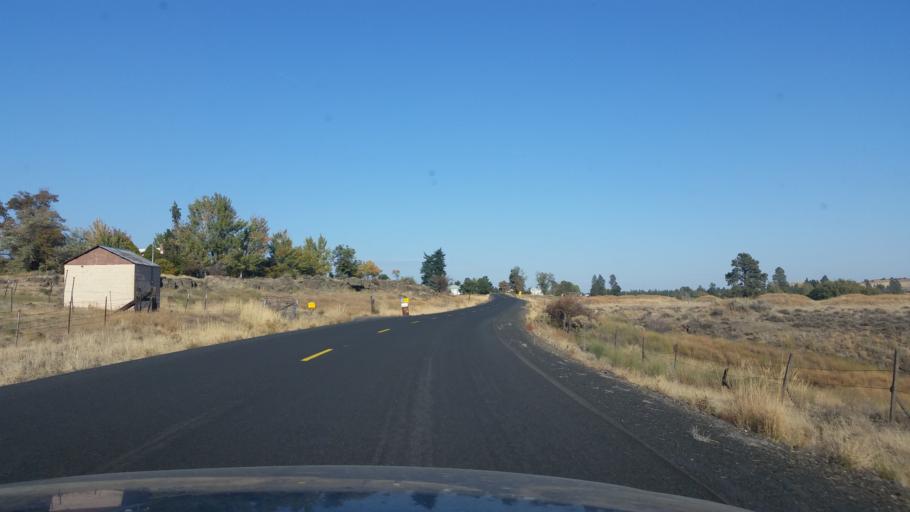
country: US
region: Washington
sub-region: Spokane County
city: Cheney
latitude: 47.3505
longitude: -117.7171
